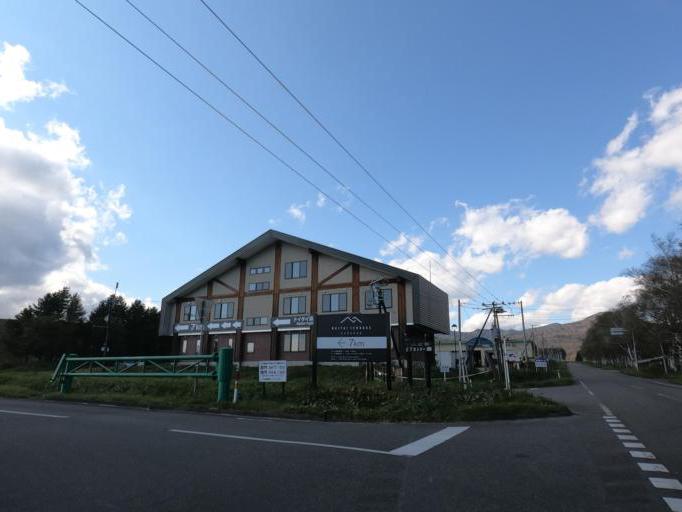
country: JP
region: Hokkaido
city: Otofuke
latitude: 43.2838
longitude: 143.2373
